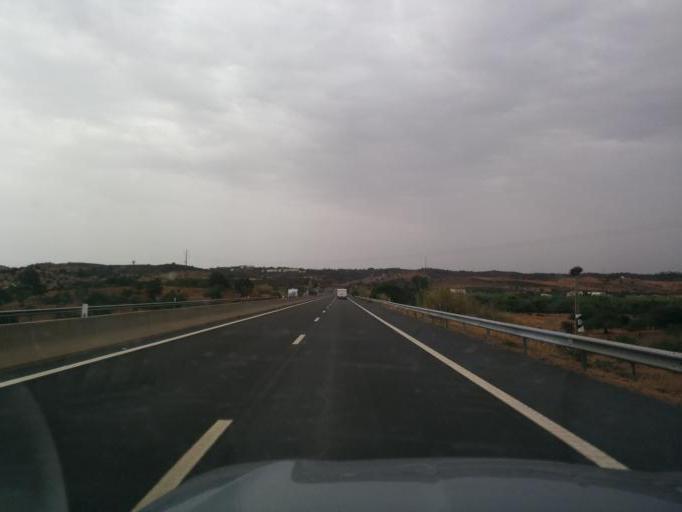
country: PT
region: Faro
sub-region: Castro Marim
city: Castro Marim
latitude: 37.2157
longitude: -7.4822
